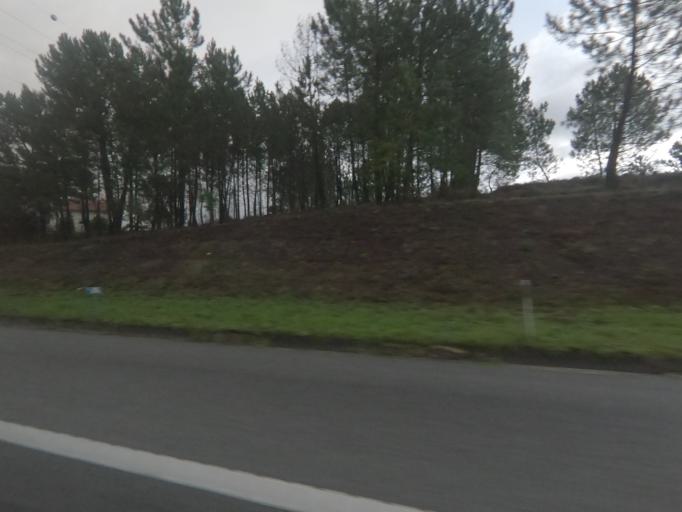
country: PT
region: Viana do Castelo
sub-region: Ponte de Lima
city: Ponte de Lima
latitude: 41.7607
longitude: -8.5605
